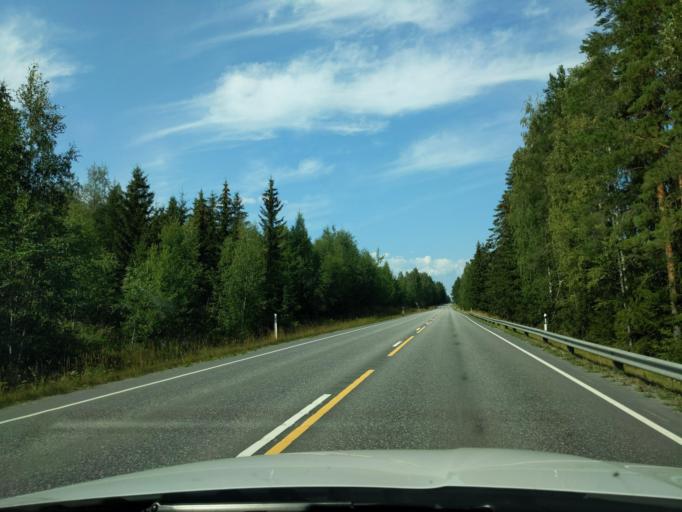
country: FI
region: Paijanne Tavastia
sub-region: Lahti
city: Padasjoki
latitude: 61.3611
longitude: 25.2220
